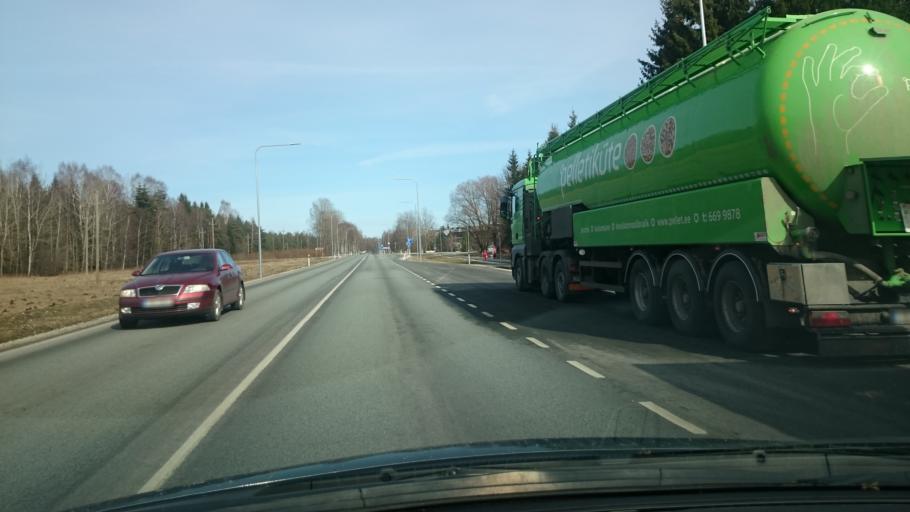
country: EE
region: Jaervamaa
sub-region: Paide linn
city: Paide
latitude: 58.8914
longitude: 25.5537
